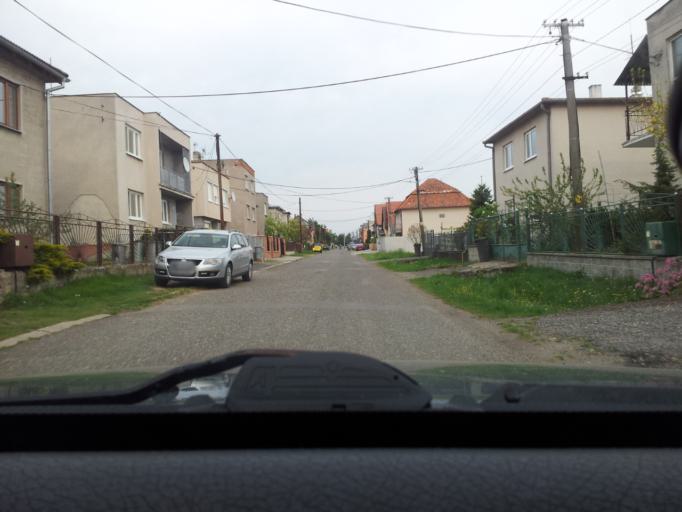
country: SK
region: Nitriansky
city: Levice
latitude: 48.2674
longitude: 18.5885
